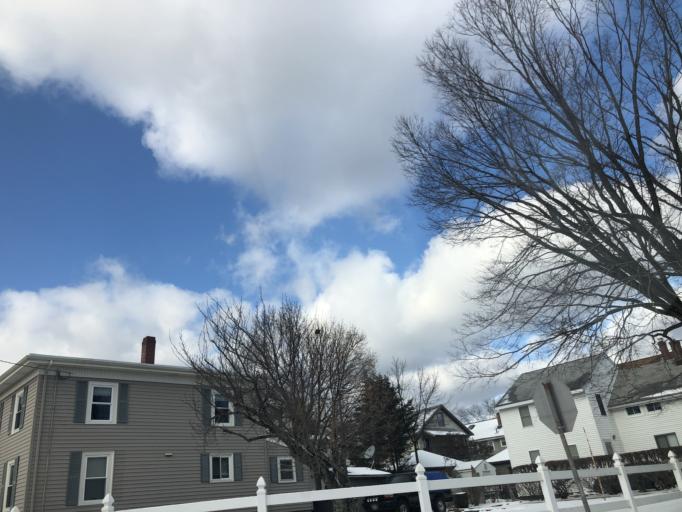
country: US
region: Massachusetts
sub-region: Middlesex County
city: Arlington
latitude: 42.4181
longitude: -71.1444
